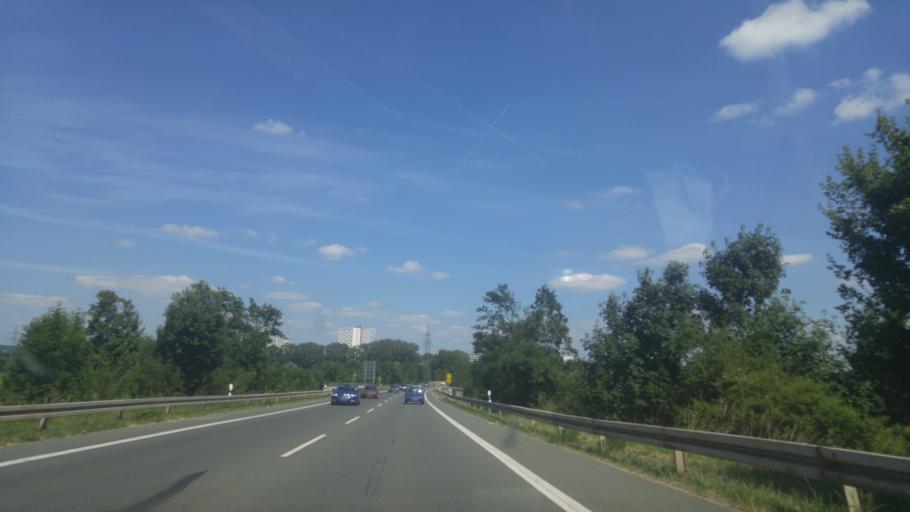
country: DE
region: Bavaria
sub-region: Regierungsbezirk Mittelfranken
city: Erlangen
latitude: 49.5755
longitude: 10.9764
